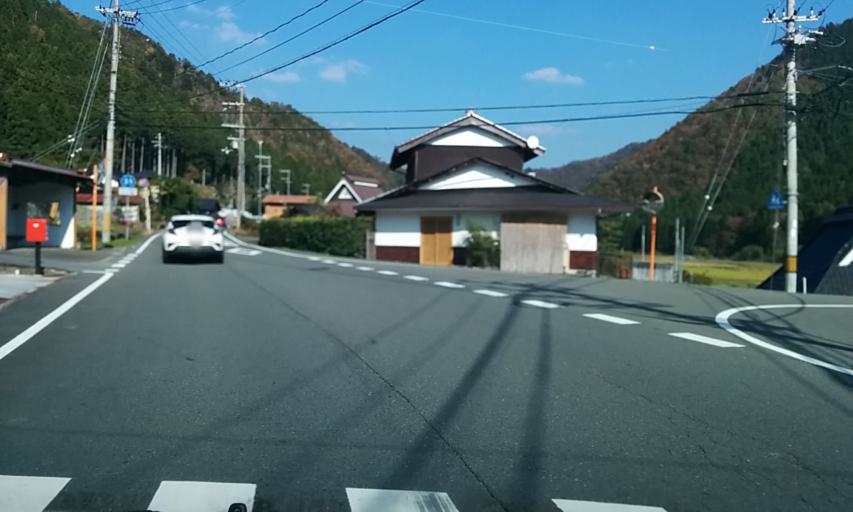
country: JP
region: Fukui
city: Obama
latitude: 35.2787
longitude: 135.5903
